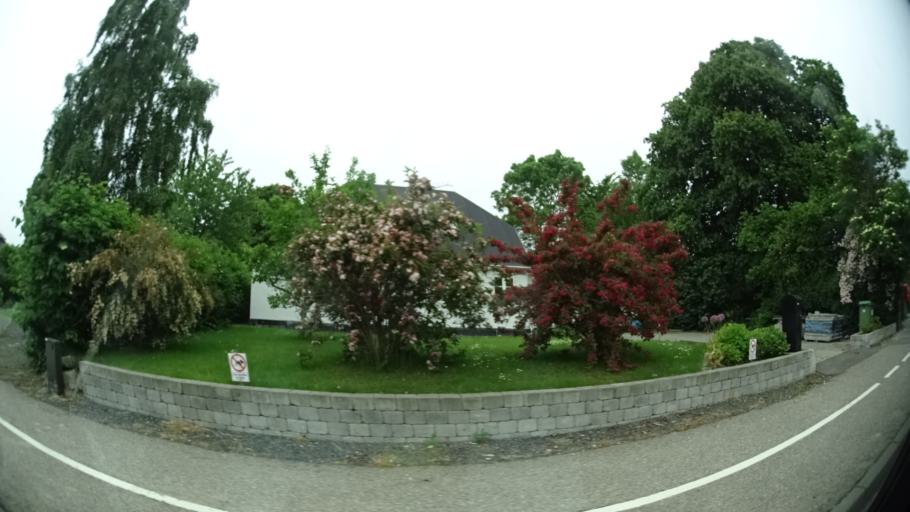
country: DK
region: Central Jutland
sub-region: Arhus Kommune
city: Logten
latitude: 56.2619
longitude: 10.3068
